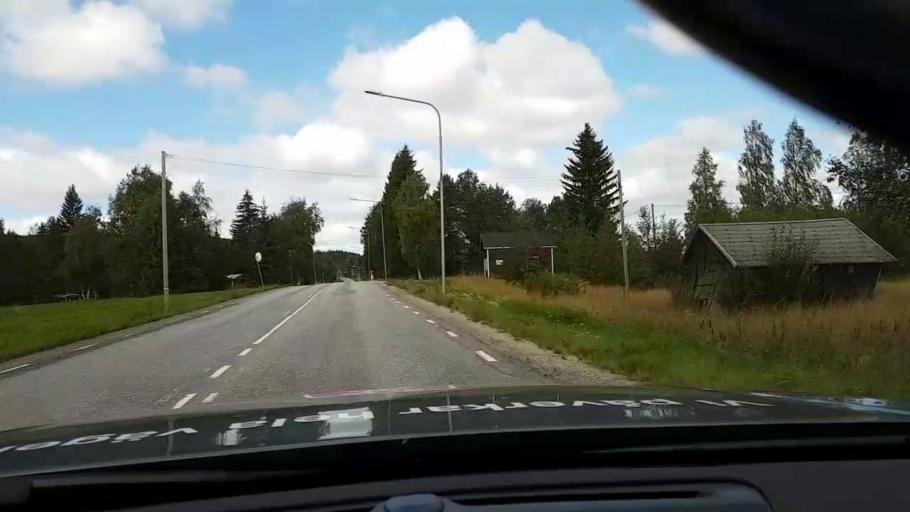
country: SE
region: Vaesternorrland
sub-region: OErnskoeldsviks Kommun
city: Bredbyn
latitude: 63.4843
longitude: 18.0879
